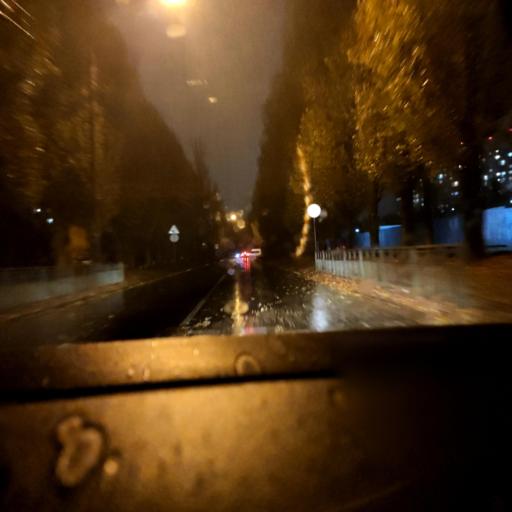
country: RU
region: Voronezj
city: Podgornoye
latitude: 51.6971
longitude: 39.1361
